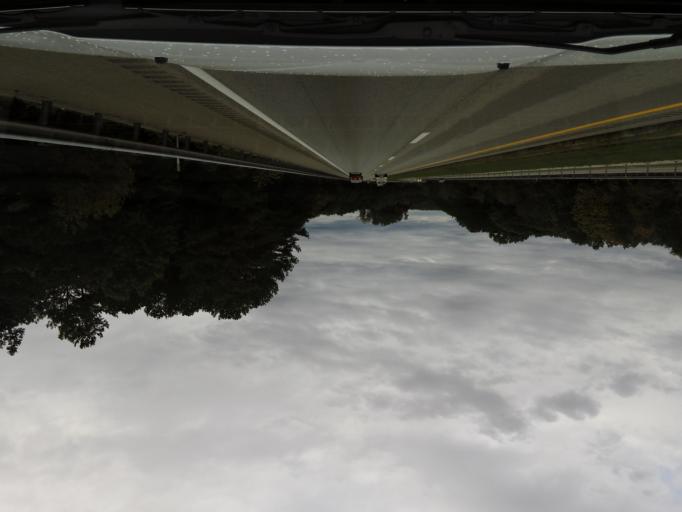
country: US
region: Kentucky
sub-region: Laurel County
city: London
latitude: 37.2124
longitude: -84.1851
